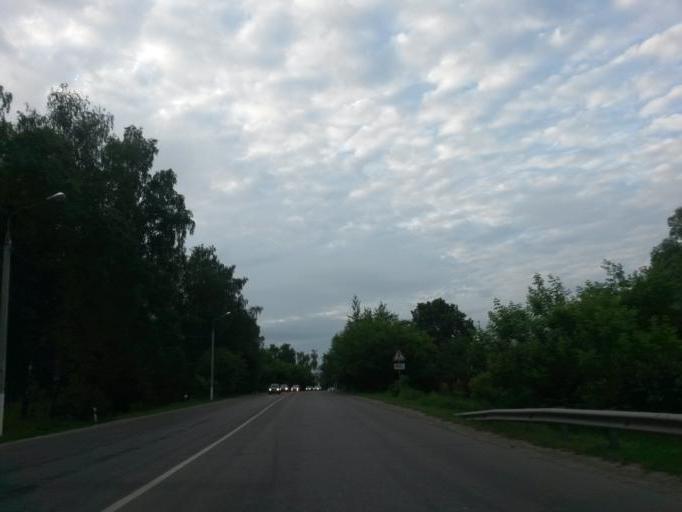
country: RU
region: Moskovskaya
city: Stolbovaya
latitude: 55.2189
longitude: 37.5029
